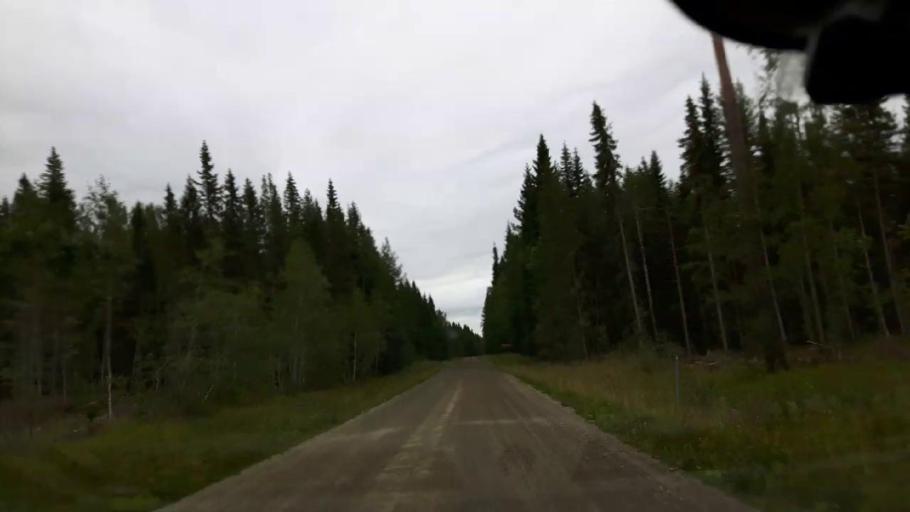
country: SE
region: Jaemtland
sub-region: Braecke Kommun
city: Braecke
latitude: 62.9797
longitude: 15.4025
